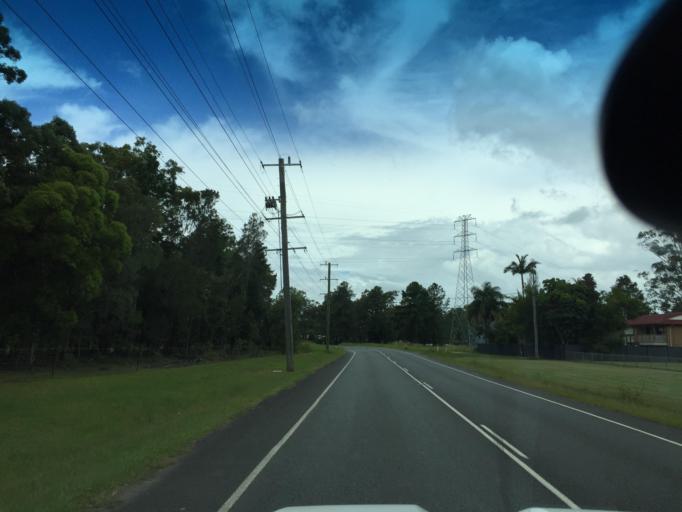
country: AU
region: Queensland
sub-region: Moreton Bay
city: Caboolture
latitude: -27.0675
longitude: 152.9144
